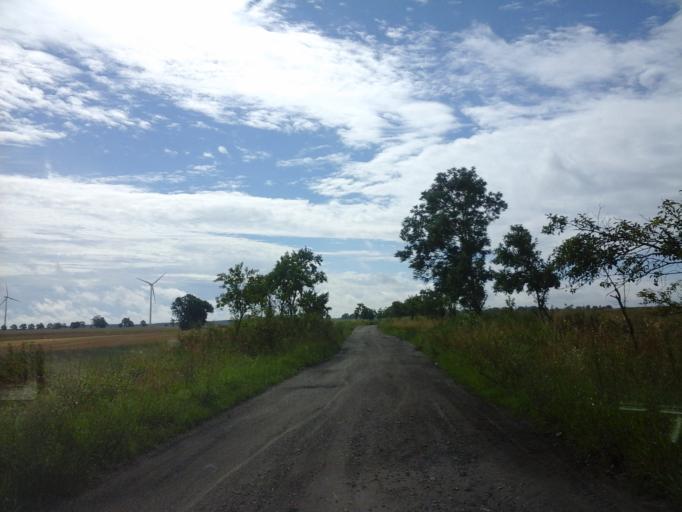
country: PL
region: West Pomeranian Voivodeship
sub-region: Powiat choszczenski
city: Krzecin
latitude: 53.0806
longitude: 15.4315
